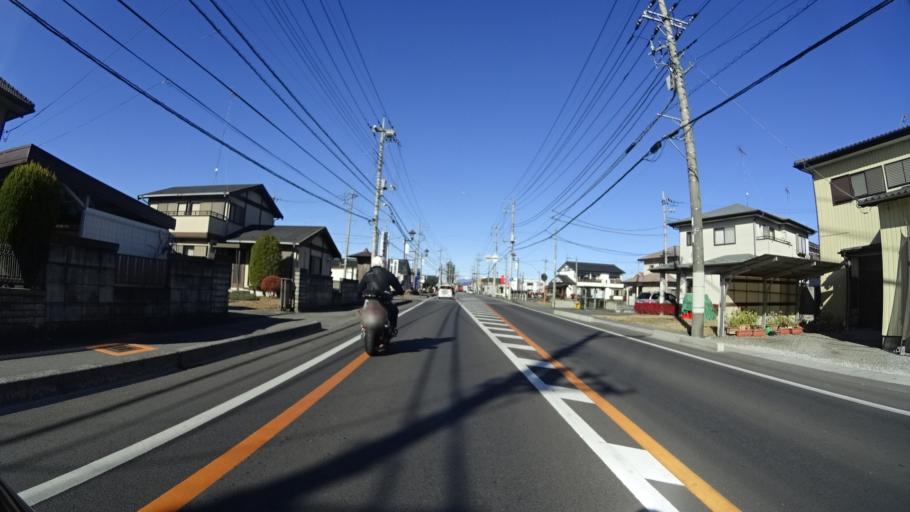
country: JP
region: Tochigi
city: Kanuma
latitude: 36.5112
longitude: 139.7516
